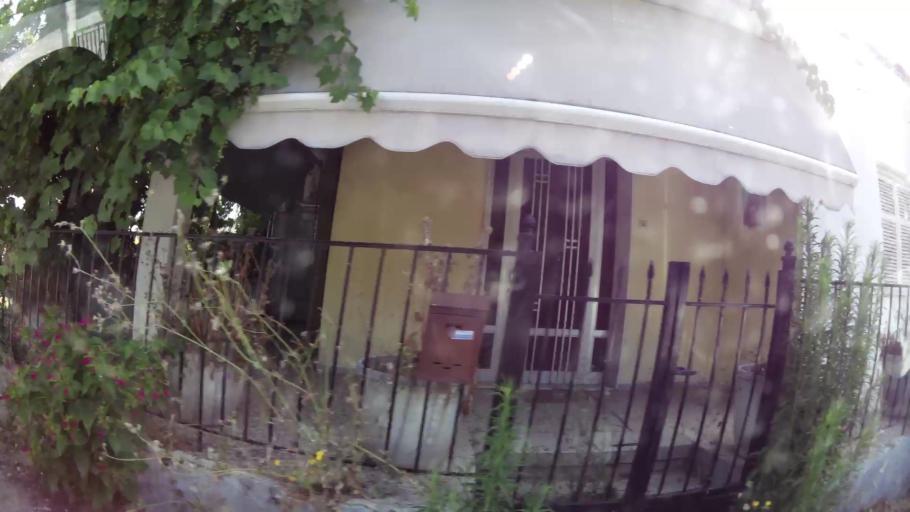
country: GR
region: Central Macedonia
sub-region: Nomos Pierias
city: Katerini
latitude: 40.2784
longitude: 22.5141
